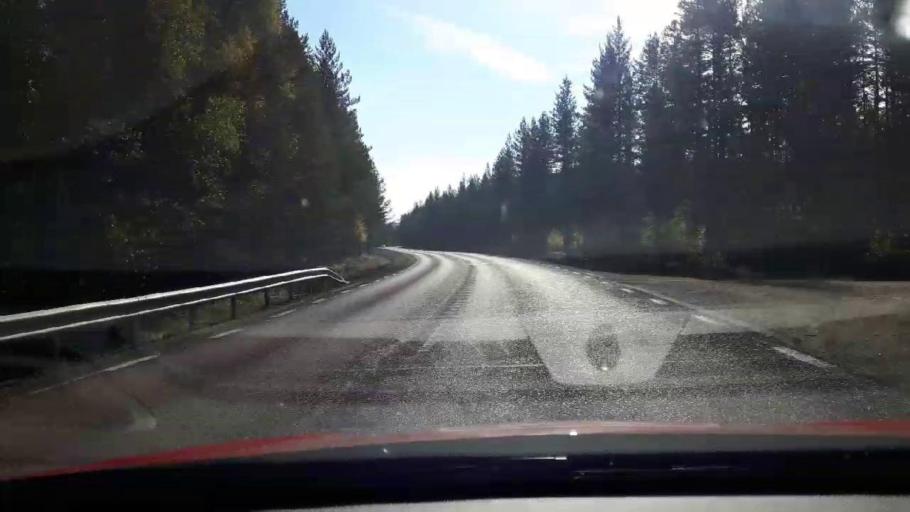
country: SE
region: Gaevleborg
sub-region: Ljusdals Kommun
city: Farila
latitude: 61.9076
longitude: 15.6308
